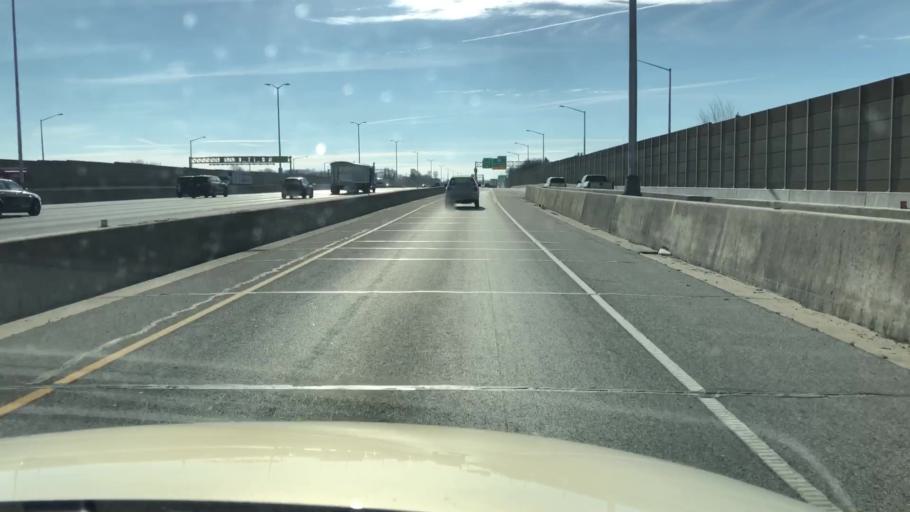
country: US
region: Wisconsin
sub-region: Milwaukee County
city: Saint Francis
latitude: 42.9534
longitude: -87.9353
